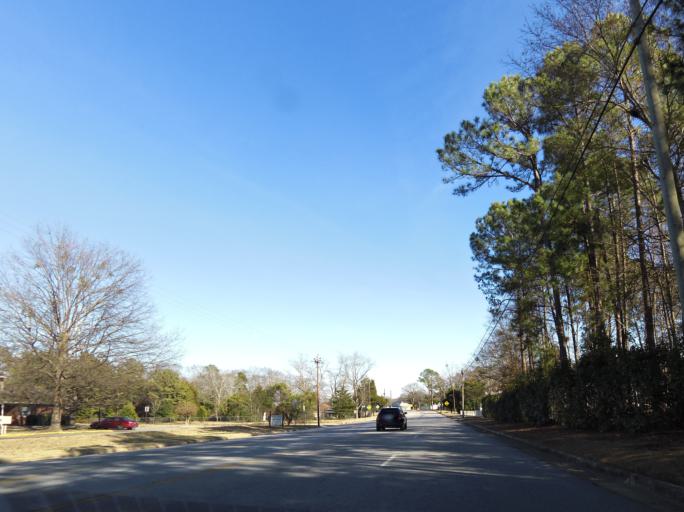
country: US
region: Georgia
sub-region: Crawford County
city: Roberta
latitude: 32.7214
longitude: -84.0172
